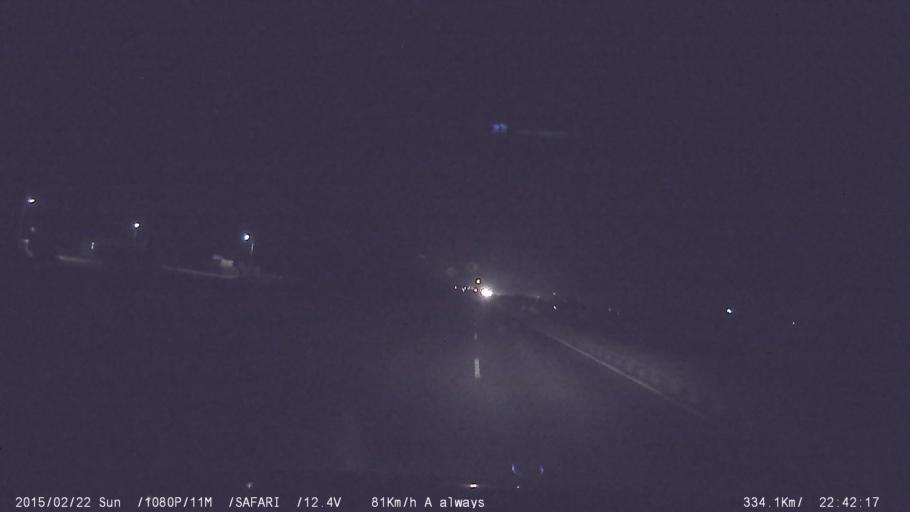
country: IN
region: Tamil Nadu
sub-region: Namakkal
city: Namakkal
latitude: 11.1873
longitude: 78.0797
